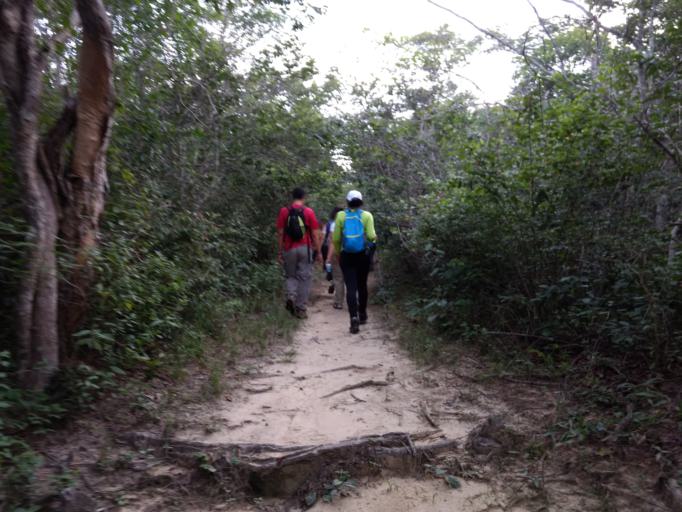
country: BR
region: Ceara
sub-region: Crateus
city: Crateus
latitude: -5.1445
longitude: -40.9230
